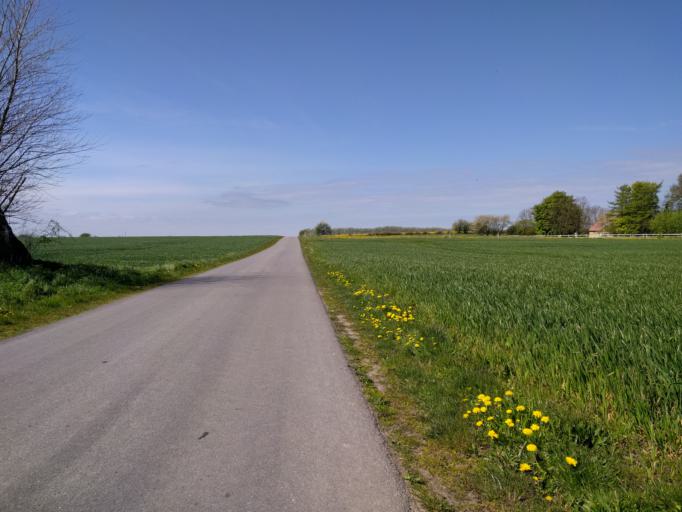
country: DK
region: South Denmark
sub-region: Kerteminde Kommune
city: Munkebo
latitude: 55.4447
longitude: 10.5992
